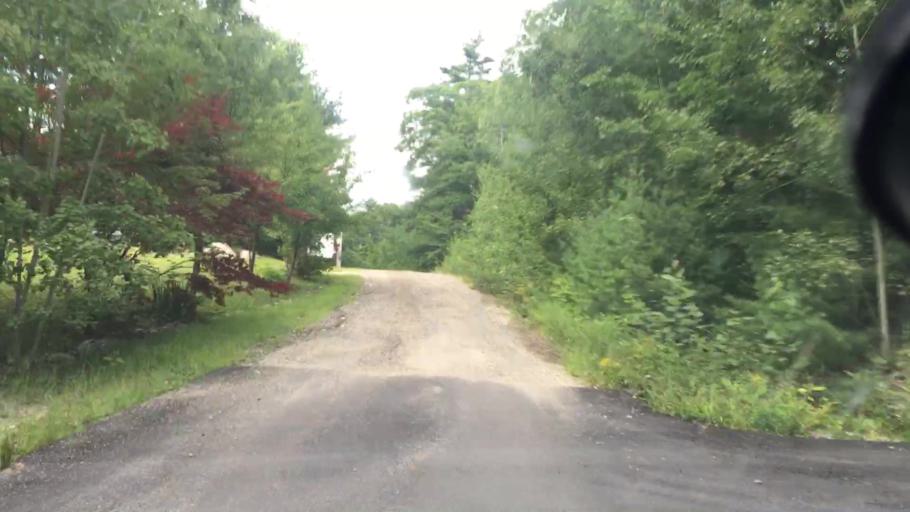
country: US
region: Maine
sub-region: Cumberland County
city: Raymond
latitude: 43.8867
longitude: -70.4551
